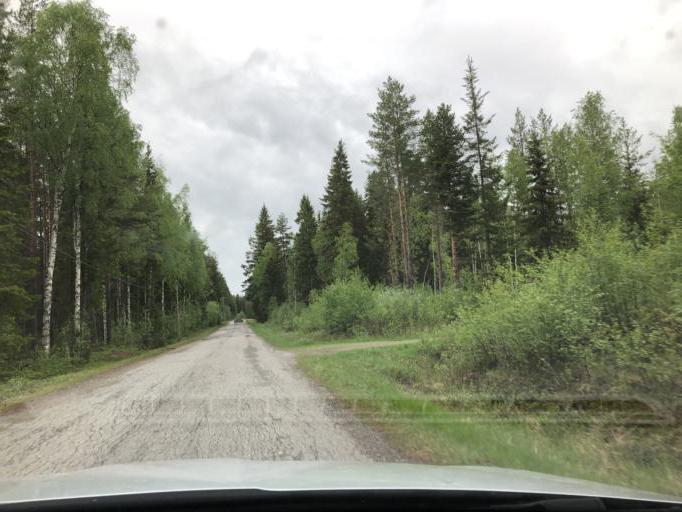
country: SE
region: Norrbotten
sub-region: Pitea Kommun
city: Roknas
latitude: 65.3831
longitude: 21.2694
